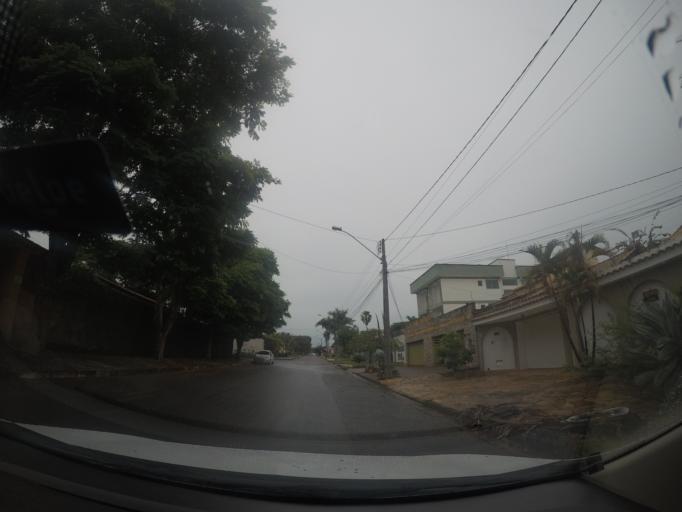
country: BR
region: Goias
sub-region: Goiania
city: Goiania
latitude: -16.6397
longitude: -49.2357
